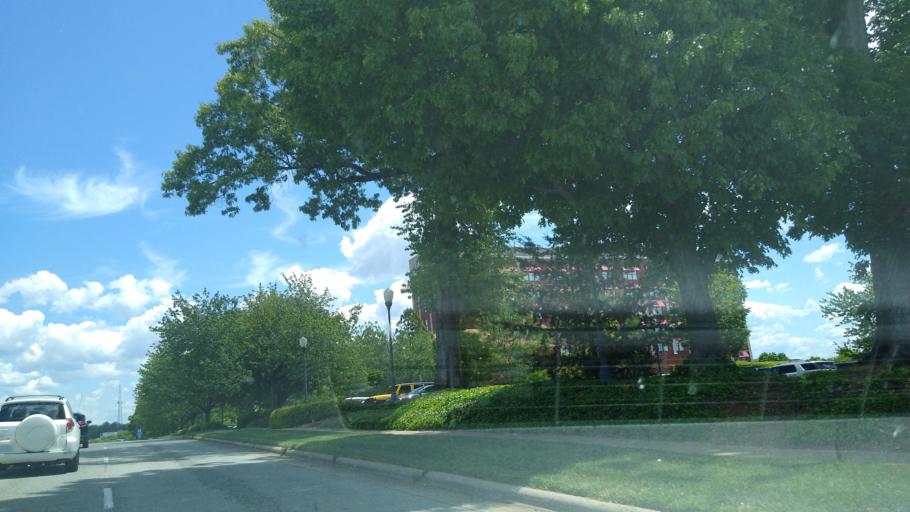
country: US
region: North Carolina
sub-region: Guilford County
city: Greensboro
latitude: 36.0863
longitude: -79.8275
